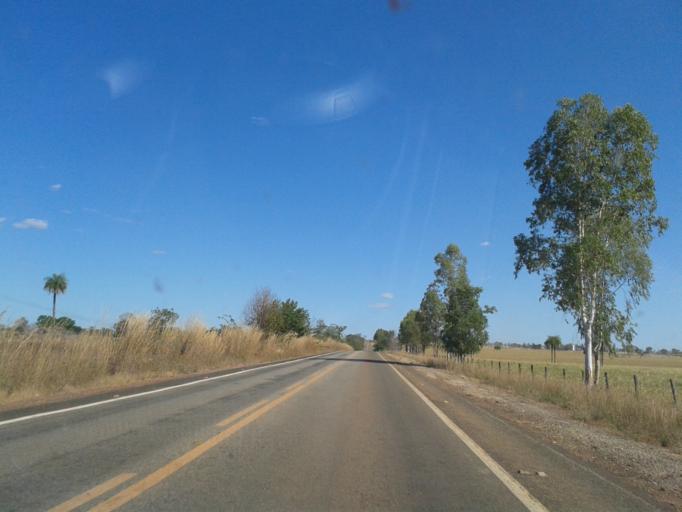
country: BR
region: Goias
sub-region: Crixas
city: Crixas
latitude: -14.2359
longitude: -50.3947
